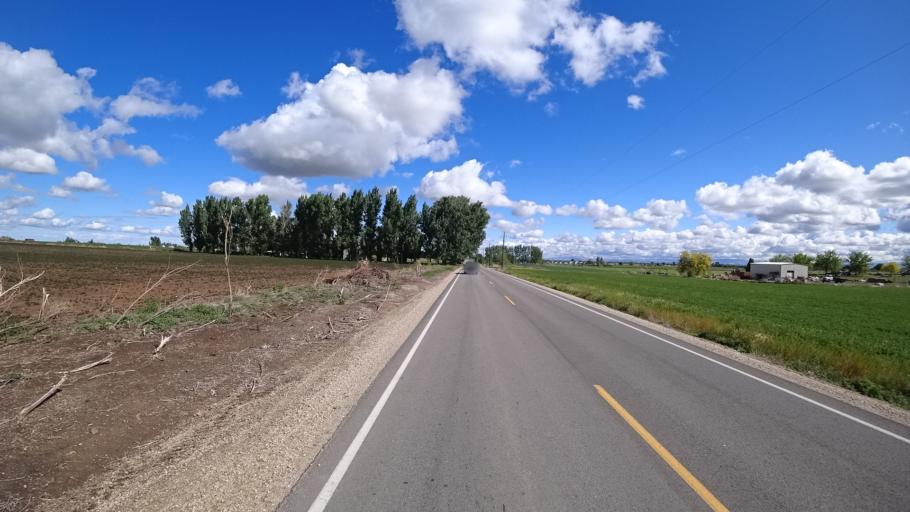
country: US
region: Idaho
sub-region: Ada County
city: Kuna
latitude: 43.4909
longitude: -116.4539
